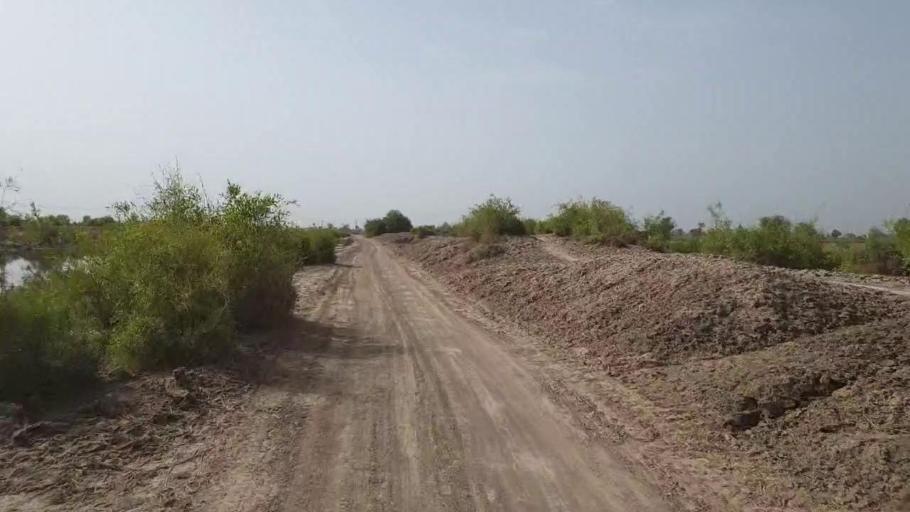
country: PK
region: Sindh
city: Daur
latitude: 26.4296
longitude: 68.1575
